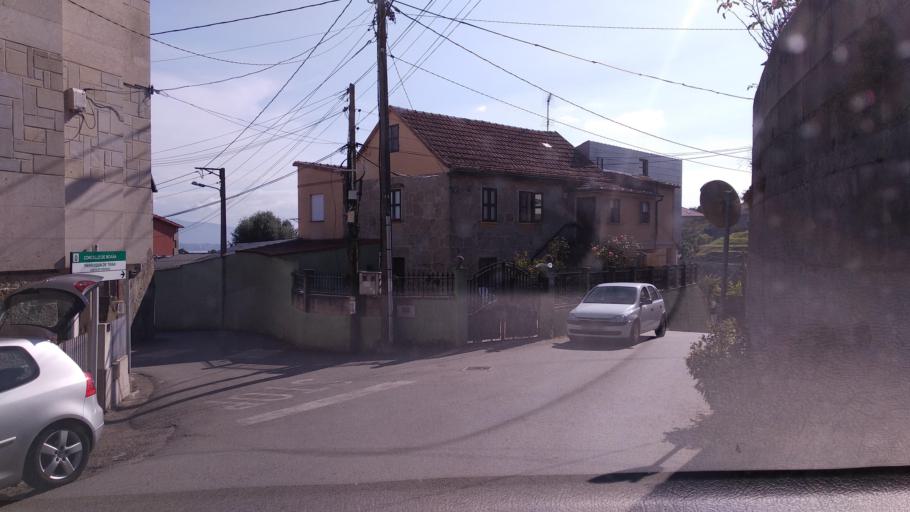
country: ES
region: Galicia
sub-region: Provincia de Pontevedra
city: Moana
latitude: 42.2802
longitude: -8.7456
